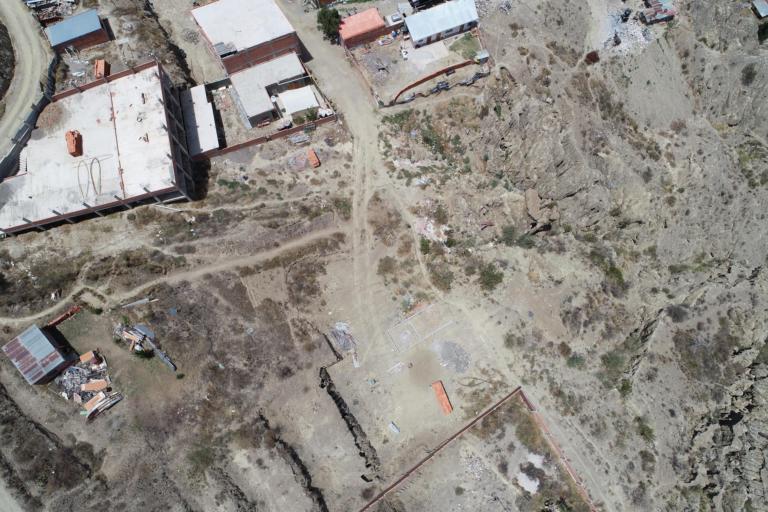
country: BO
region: La Paz
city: La Paz
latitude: -16.5192
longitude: -68.0789
